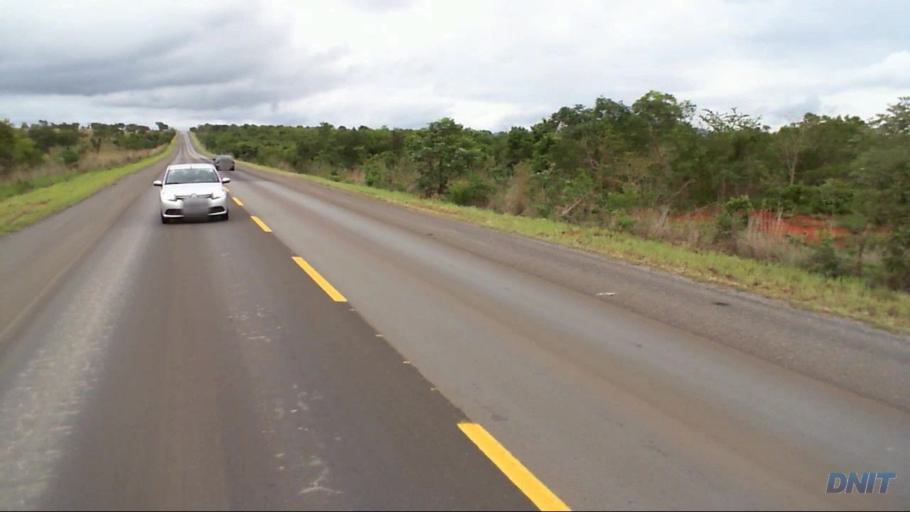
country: BR
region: Goias
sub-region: Padre Bernardo
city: Padre Bernardo
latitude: -15.2184
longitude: -48.5523
